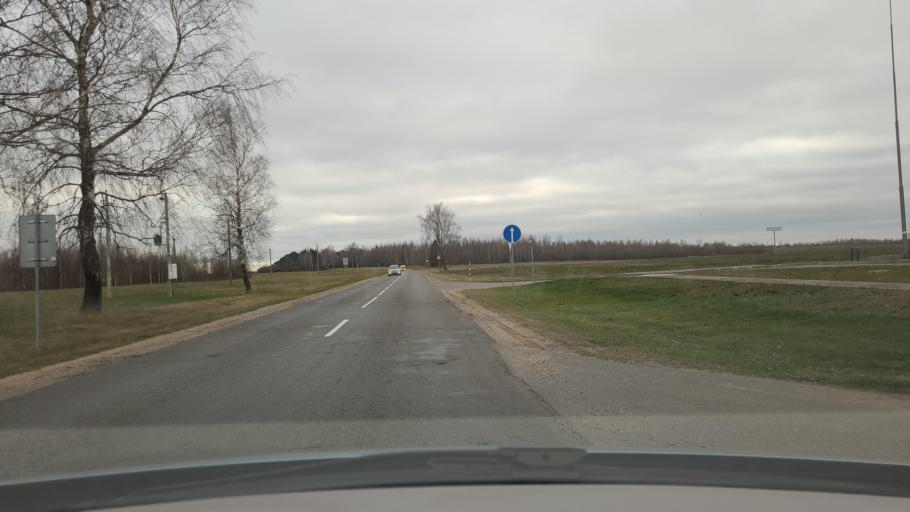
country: BY
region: Minsk
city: Khalopyenichy
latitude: 54.5025
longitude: 28.9569
